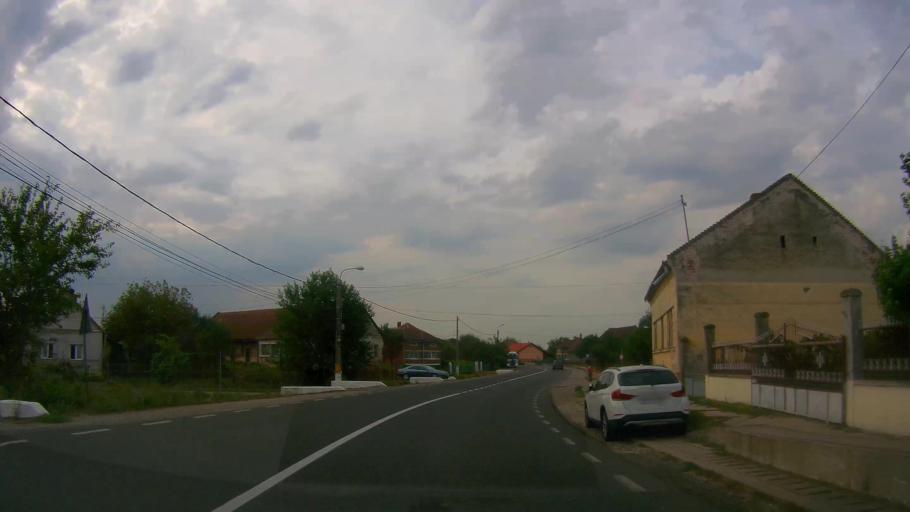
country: RO
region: Satu Mare
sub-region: Comuna Beltiug
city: Beltiug
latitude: 47.5820
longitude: 22.8804
